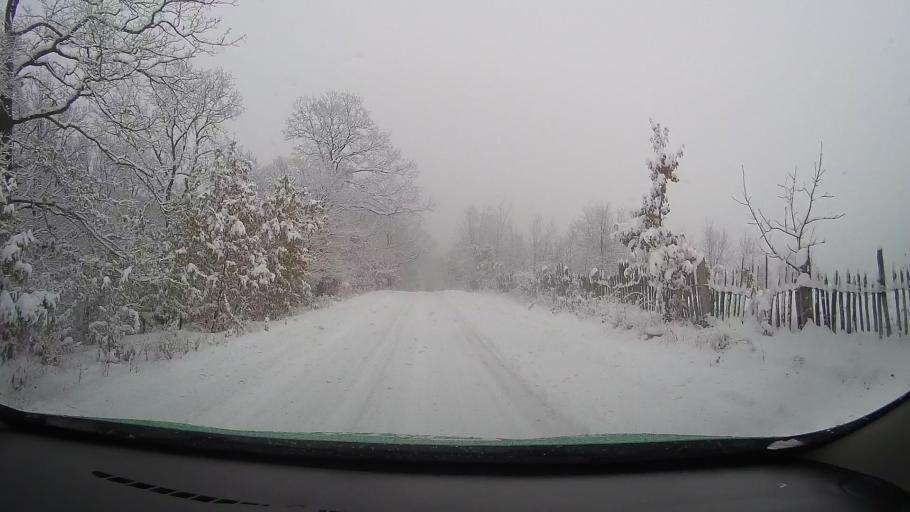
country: RO
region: Hunedoara
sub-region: Comuna Teliucu Inferior
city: Teliucu Inferior
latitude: 45.6903
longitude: 22.8942
